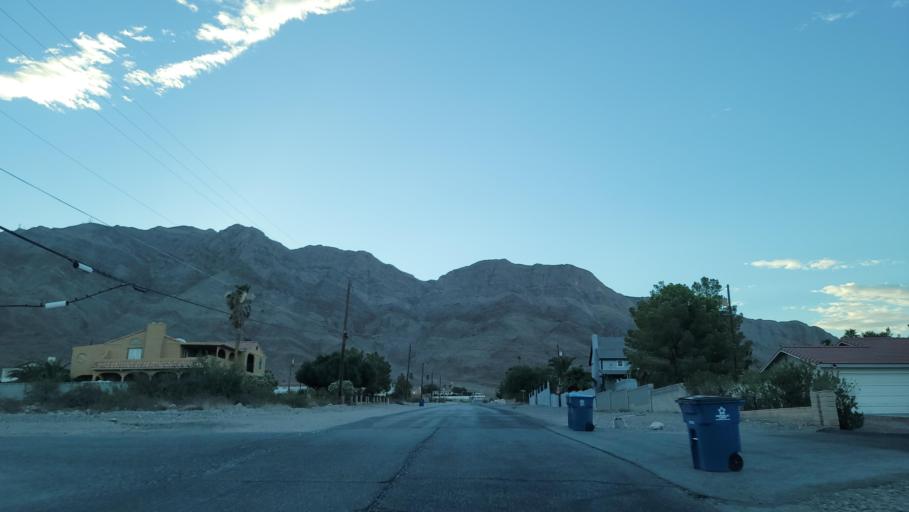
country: US
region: Nevada
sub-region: Clark County
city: Sunrise Manor
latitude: 36.1665
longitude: -115.0210
